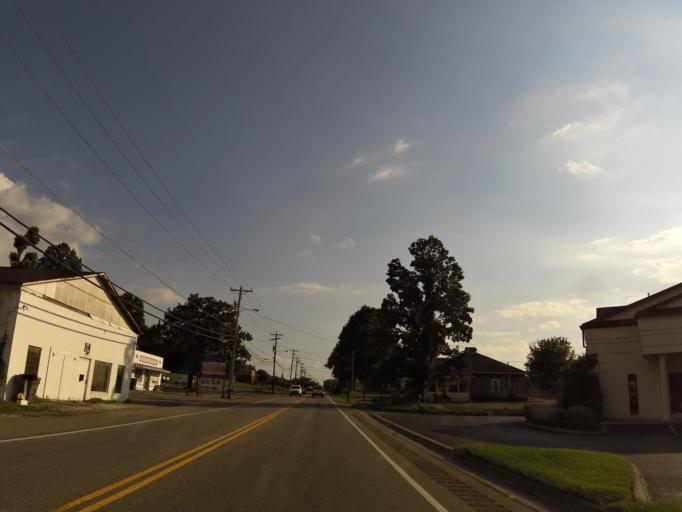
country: US
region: Tennessee
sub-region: Blount County
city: Maryville
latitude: 35.7740
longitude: -83.9555
